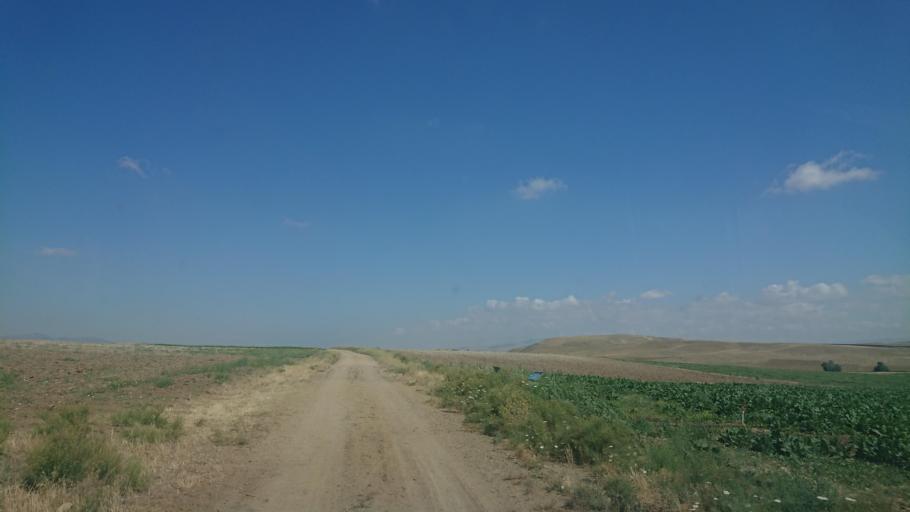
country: TR
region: Aksaray
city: Sariyahsi
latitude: 38.9659
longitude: 33.9242
